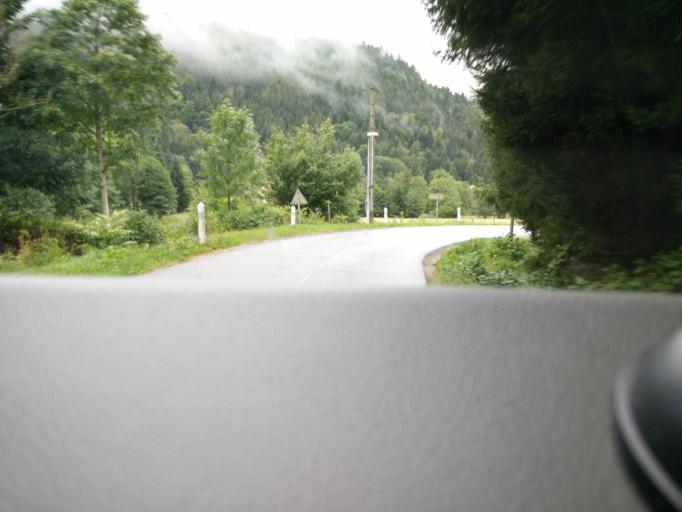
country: FR
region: Lorraine
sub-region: Departement des Vosges
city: Plainfaing
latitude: 48.1241
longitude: 7.0304
